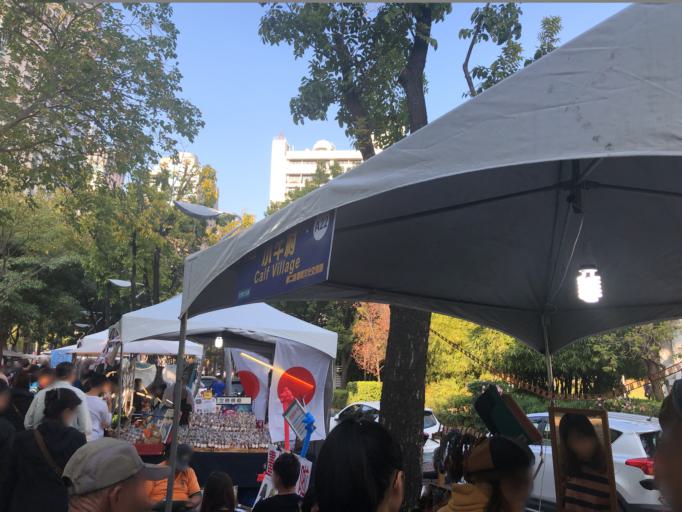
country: TW
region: Taiwan
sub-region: Taichung City
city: Taichung
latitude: 24.1524
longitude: 120.6634
